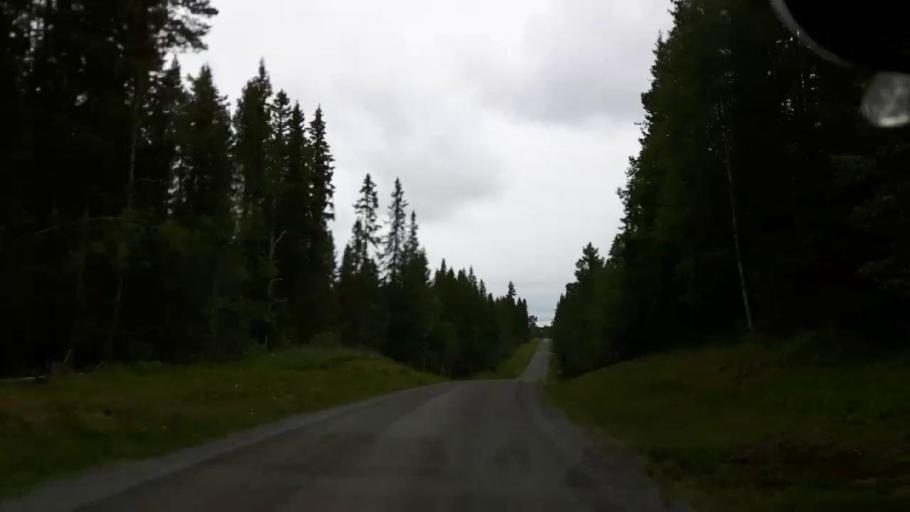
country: SE
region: Jaemtland
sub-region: OEstersunds Kommun
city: Ostersund
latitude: 63.0977
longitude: 14.5456
